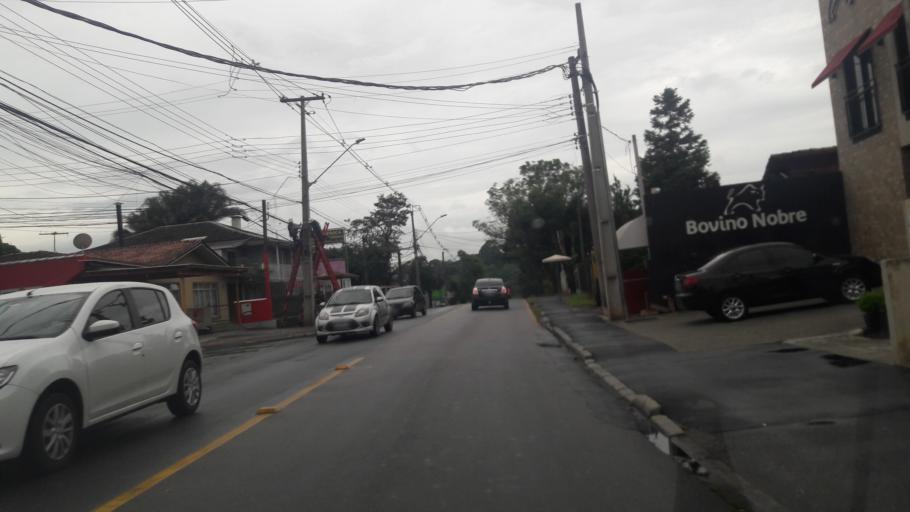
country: BR
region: Parana
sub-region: Curitiba
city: Curitiba
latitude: -25.3999
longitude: -49.3265
